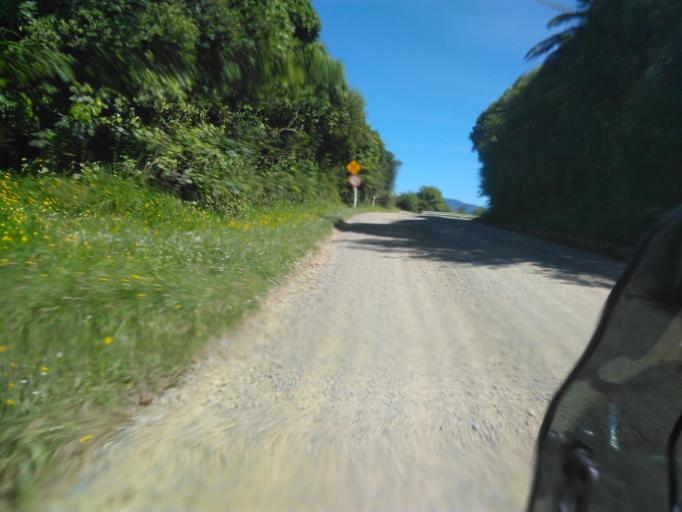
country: NZ
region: Hawke's Bay
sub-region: Wairoa District
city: Wairoa
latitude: -38.7940
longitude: 177.1248
